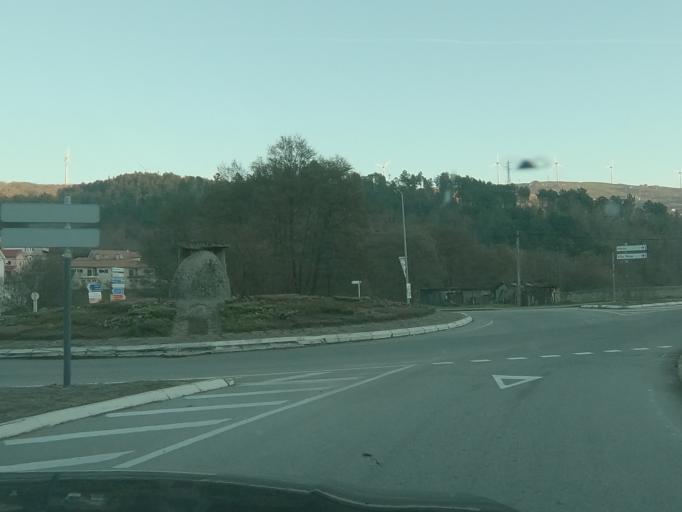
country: PT
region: Vila Real
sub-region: Vila Pouca de Aguiar
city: Vila Pouca de Aguiar
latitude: 41.4902
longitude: -7.6492
